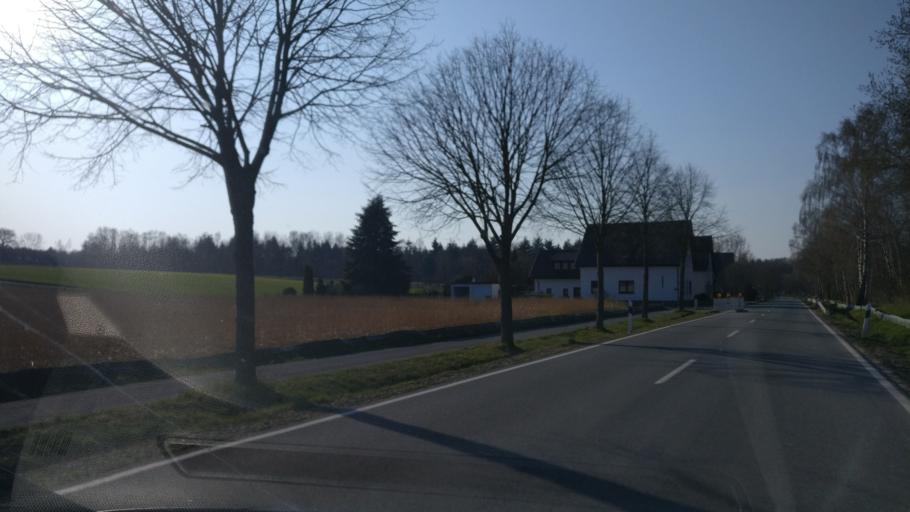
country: DE
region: North Rhine-Westphalia
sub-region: Regierungsbezirk Detmold
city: Lage
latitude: 51.9998
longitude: 8.7717
